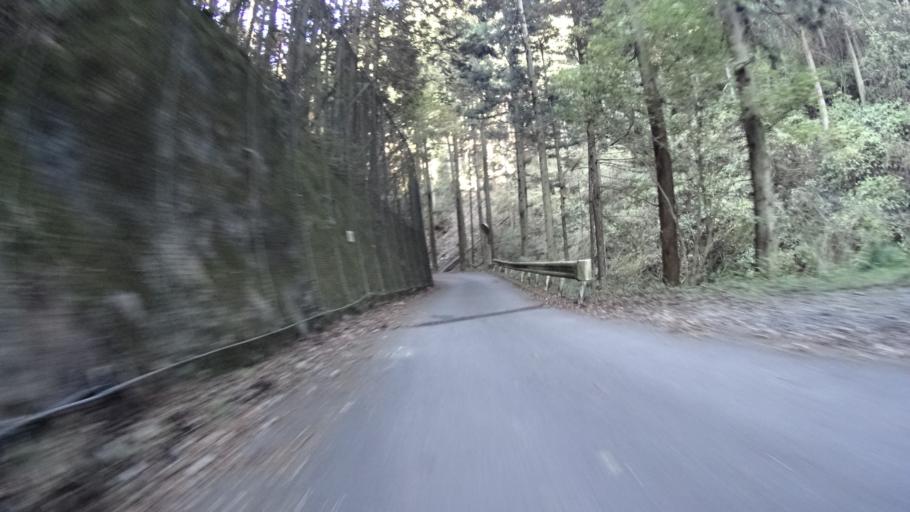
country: JP
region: Tokyo
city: Itsukaichi
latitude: 35.6598
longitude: 139.1799
